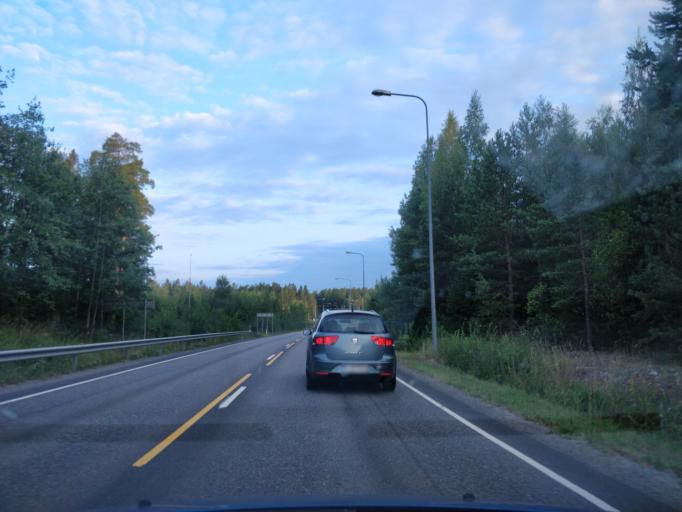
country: FI
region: Uusimaa
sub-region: Helsinki
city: Kerava
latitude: 60.3846
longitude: 25.1508
